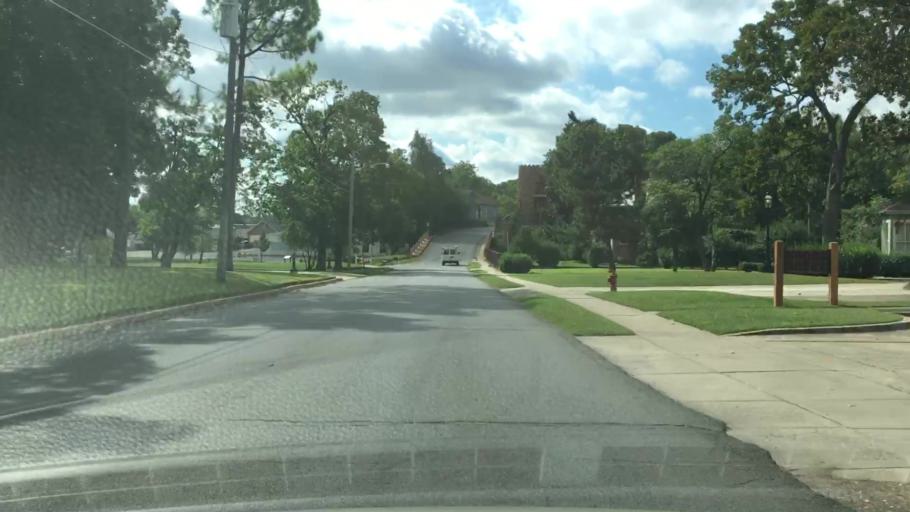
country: US
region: Oklahoma
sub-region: Cherokee County
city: Tahlequah
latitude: 35.9191
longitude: -94.9706
